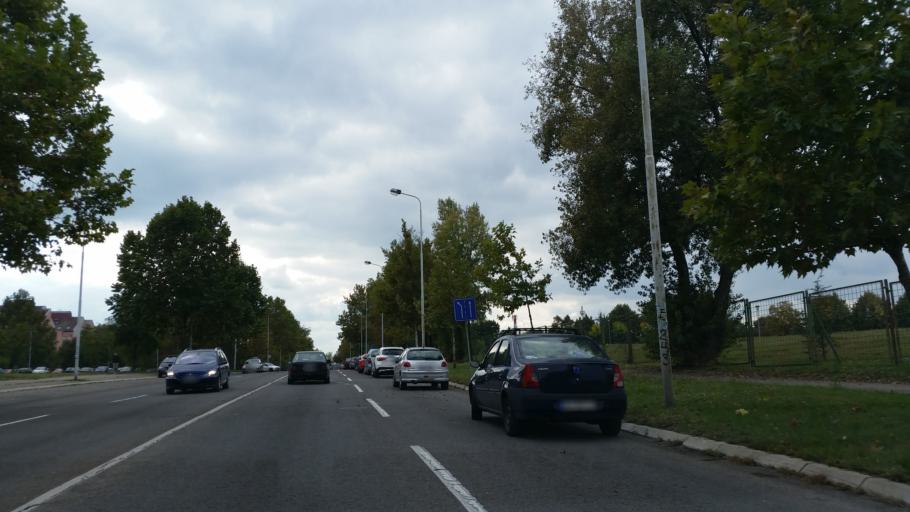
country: RS
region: Central Serbia
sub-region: Belgrade
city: Zemun
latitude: 44.8199
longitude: 20.3729
